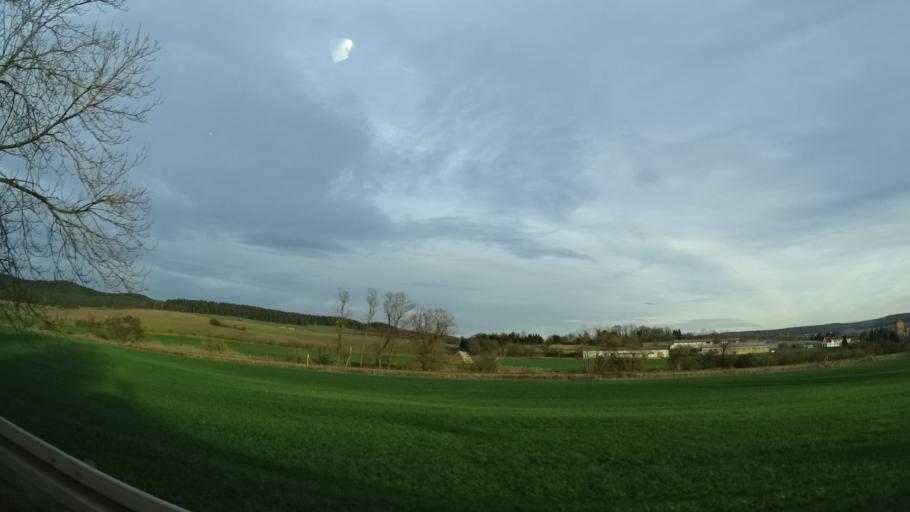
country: DE
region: Thuringia
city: Possneck
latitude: 50.7115
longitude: 11.6080
